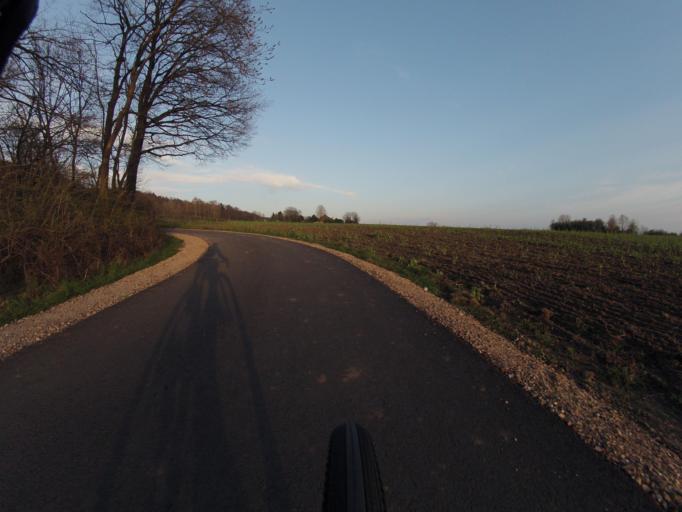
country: DE
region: North Rhine-Westphalia
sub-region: Regierungsbezirk Munster
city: Birgte
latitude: 52.2475
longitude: 7.6819
